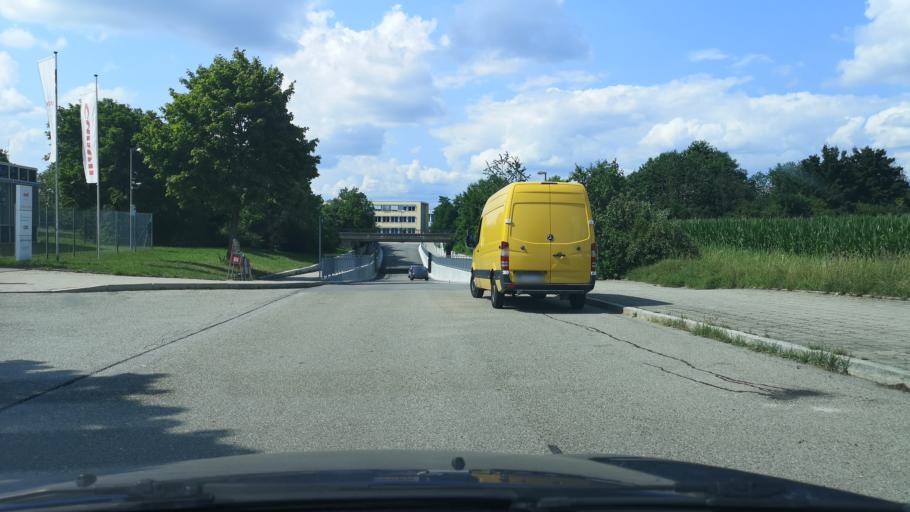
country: DE
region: Bavaria
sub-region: Upper Bavaria
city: Poing
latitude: 48.1683
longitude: 11.8019
